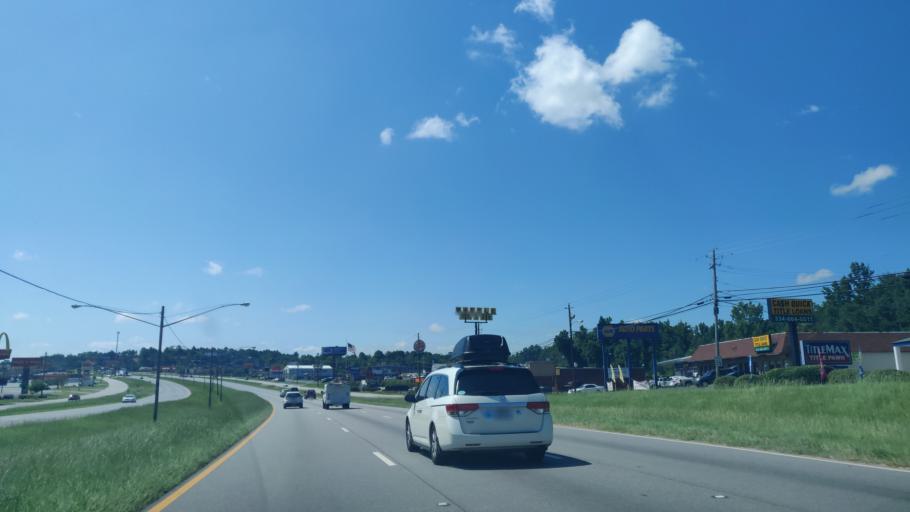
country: US
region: Alabama
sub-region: Russell County
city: Phenix City
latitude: 32.4709
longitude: -85.0297
